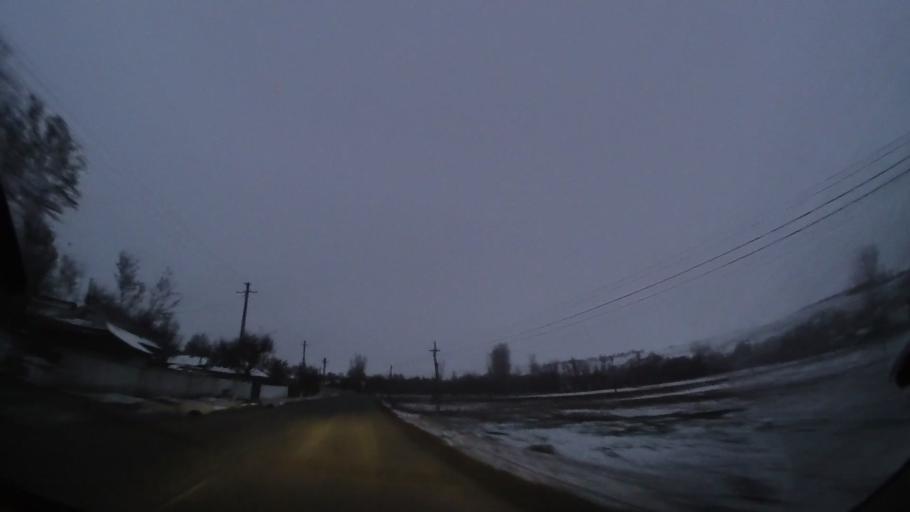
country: RO
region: Vaslui
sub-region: Comuna Dimitrie Cantemir
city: Dimitrie Cantemir
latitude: 46.5024
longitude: 28.0549
